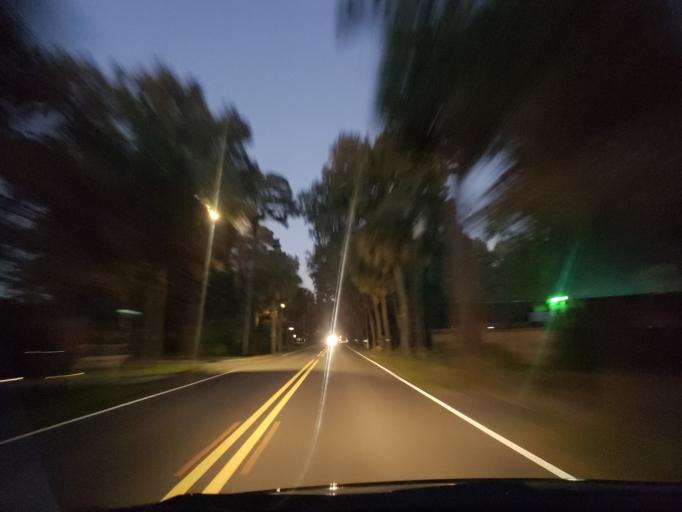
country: US
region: Georgia
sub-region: Chatham County
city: Isle of Hope
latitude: 31.9908
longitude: -81.0686
